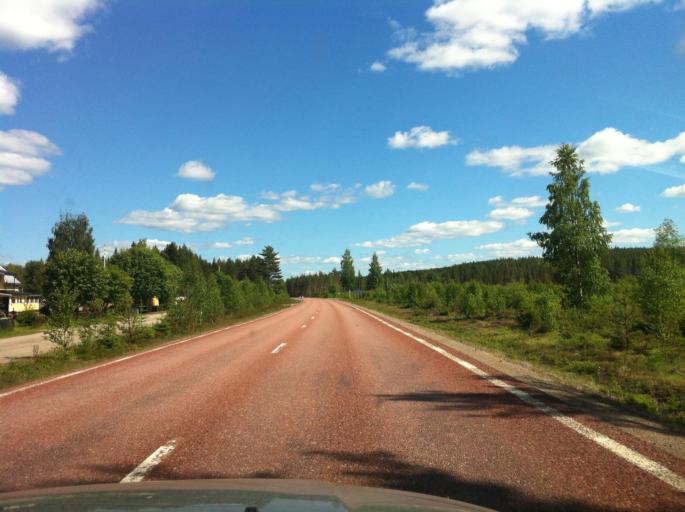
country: SE
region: Gaevleborg
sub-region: Ljusdals Kommun
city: Farila
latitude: 61.9322
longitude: 15.5355
